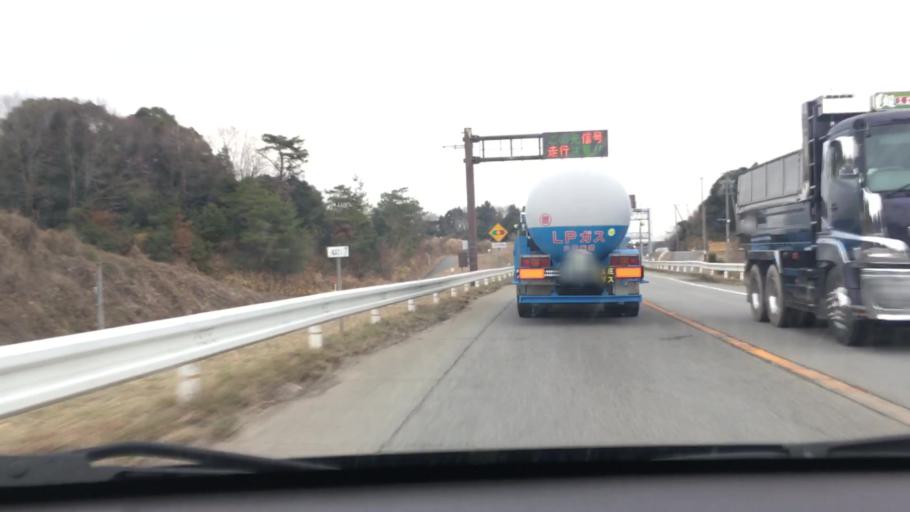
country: JP
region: Mie
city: Kameyama
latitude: 34.8646
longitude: 136.4463
